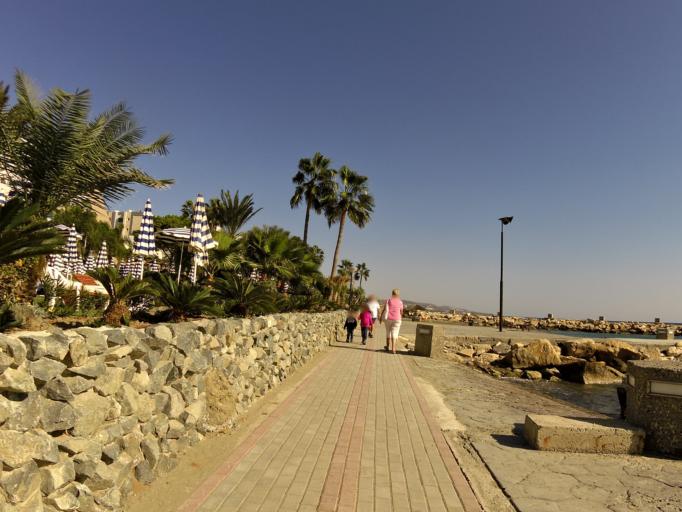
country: CY
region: Larnaka
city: Agios Tychon
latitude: 34.7083
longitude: 33.1324
